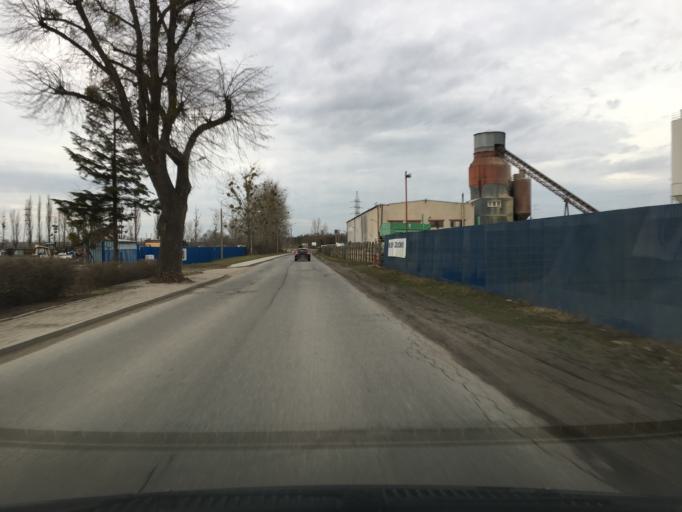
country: PL
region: Opole Voivodeship
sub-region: Powiat kedzierzynsko-kozielski
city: Kozle
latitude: 50.3495
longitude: 18.1420
